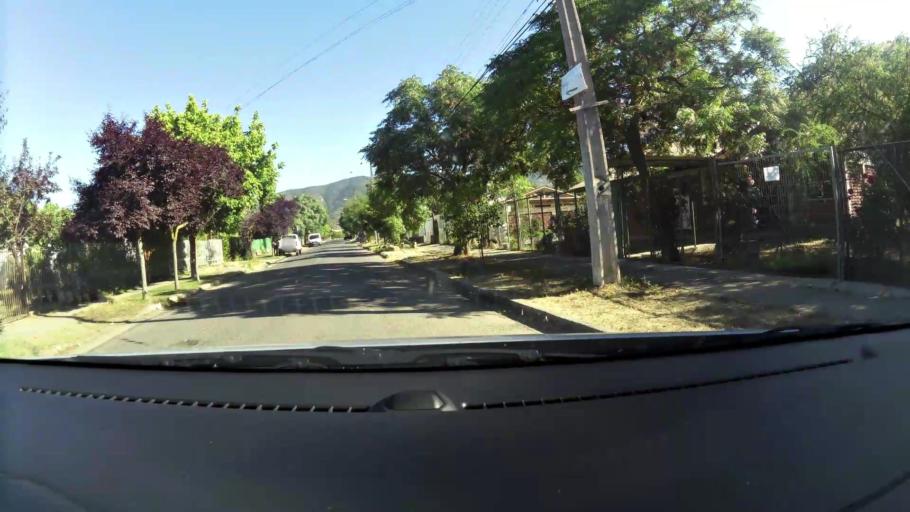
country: CL
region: Santiago Metropolitan
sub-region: Provincia de Chacabuco
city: Lampa
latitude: -33.3987
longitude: -71.1217
